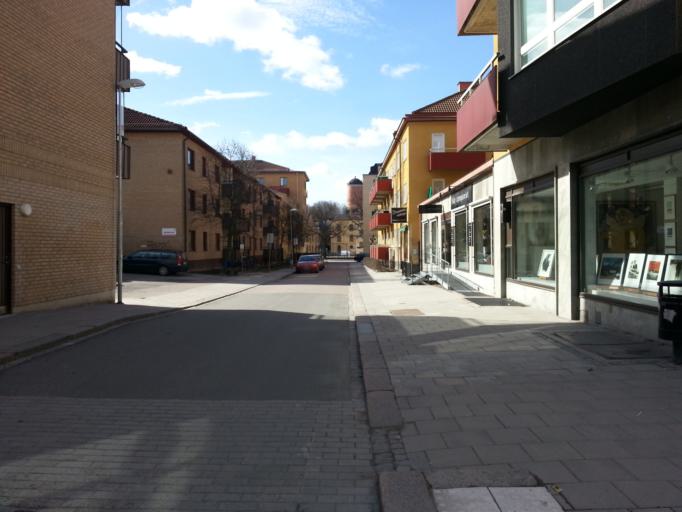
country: SE
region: Uppsala
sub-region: Uppsala Kommun
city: Uppsala
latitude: 59.8564
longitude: 17.6431
